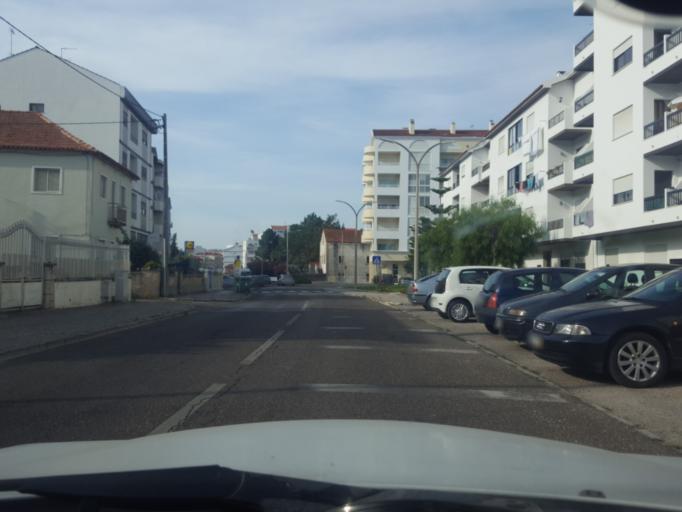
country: PT
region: Leiria
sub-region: Leiria
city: Leiria
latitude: 39.7297
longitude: -8.7979
